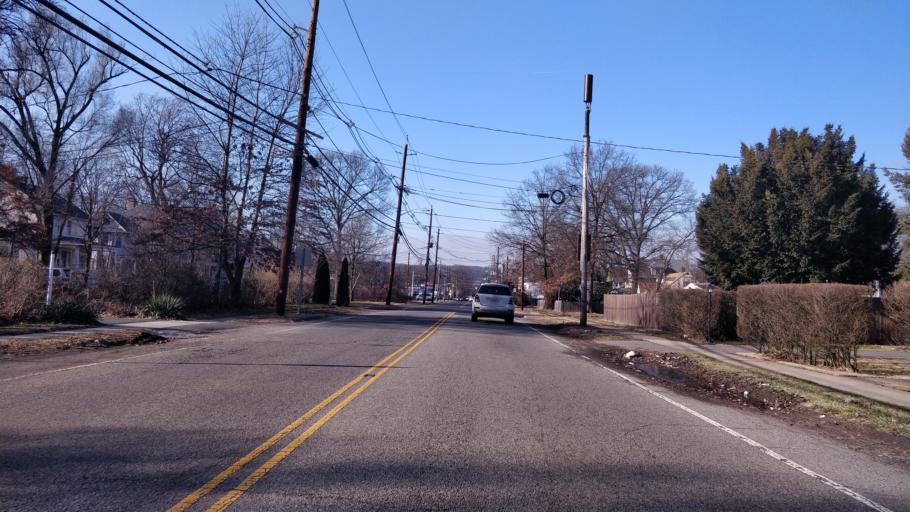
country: US
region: New Jersey
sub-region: Middlesex County
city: South Plainfield
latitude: 40.5956
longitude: -74.4350
